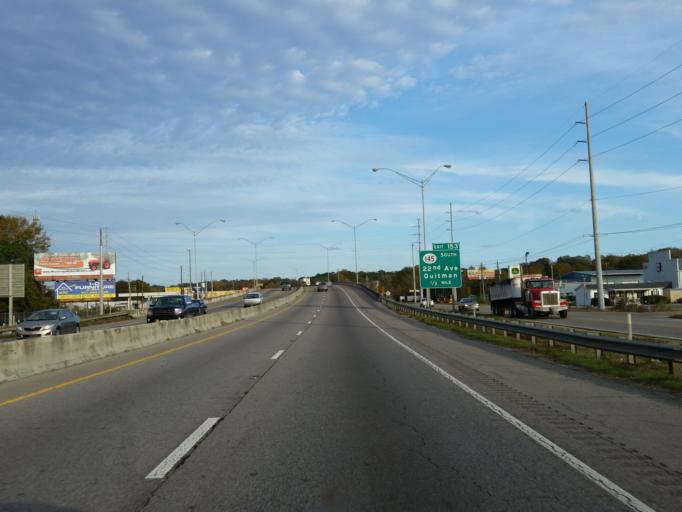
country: US
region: Mississippi
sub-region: Lauderdale County
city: Meridian
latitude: 32.3490
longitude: -88.7041
